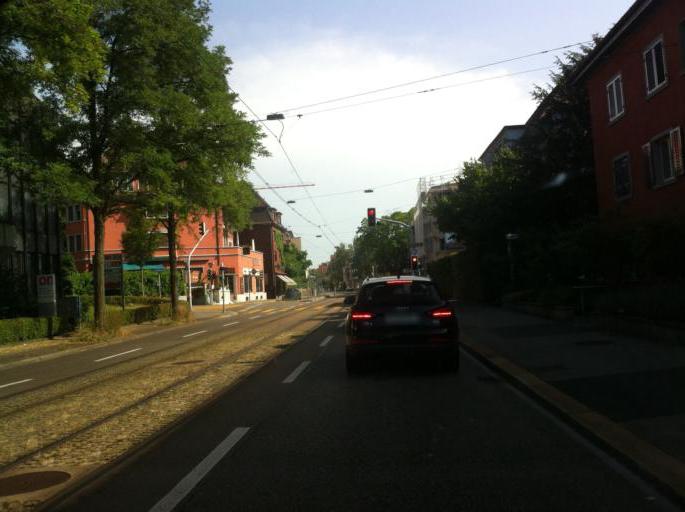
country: CH
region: Zurich
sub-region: Bezirk Zuerich
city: Zuerich (Kreis 6)
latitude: 47.3915
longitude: 8.5452
